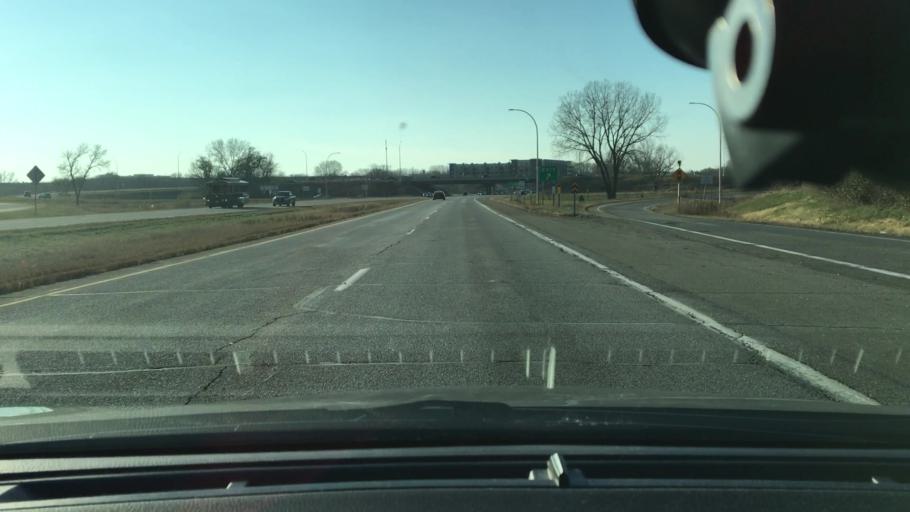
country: US
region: Minnesota
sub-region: Hennepin County
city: Golden Valley
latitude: 44.9838
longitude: -93.3964
